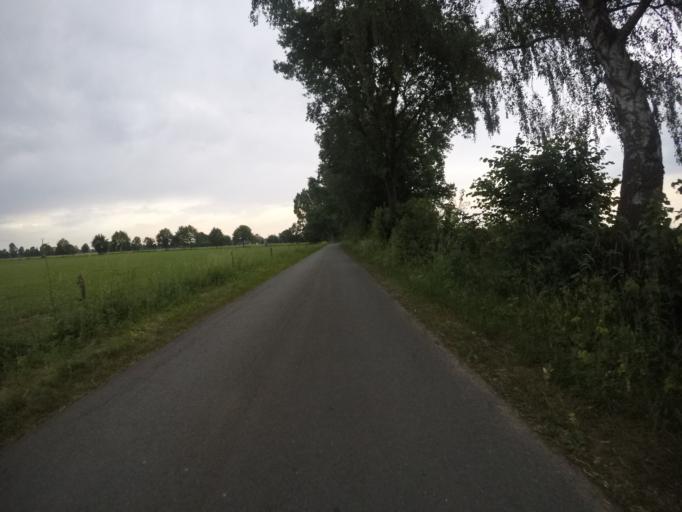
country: DE
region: North Rhine-Westphalia
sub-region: Regierungsbezirk Munster
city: Isselburg
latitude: 51.8359
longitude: 6.5396
